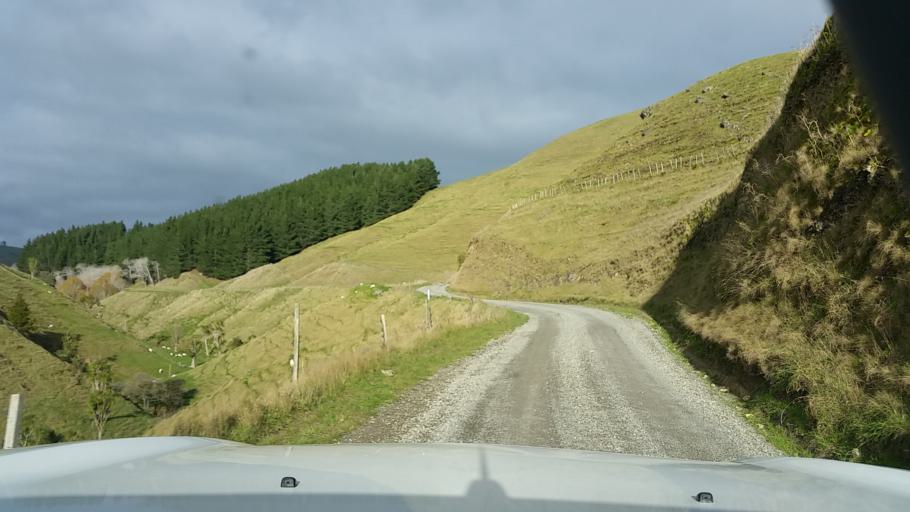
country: NZ
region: Wellington
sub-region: Masterton District
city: Masterton
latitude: -41.0363
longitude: 175.7134
